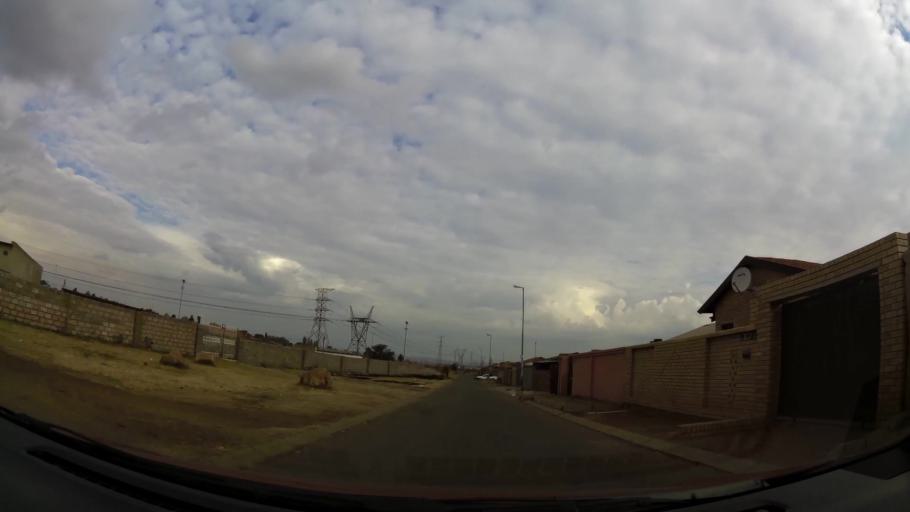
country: ZA
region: Gauteng
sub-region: City of Johannesburg Metropolitan Municipality
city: Soweto
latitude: -26.2468
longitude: 27.8370
